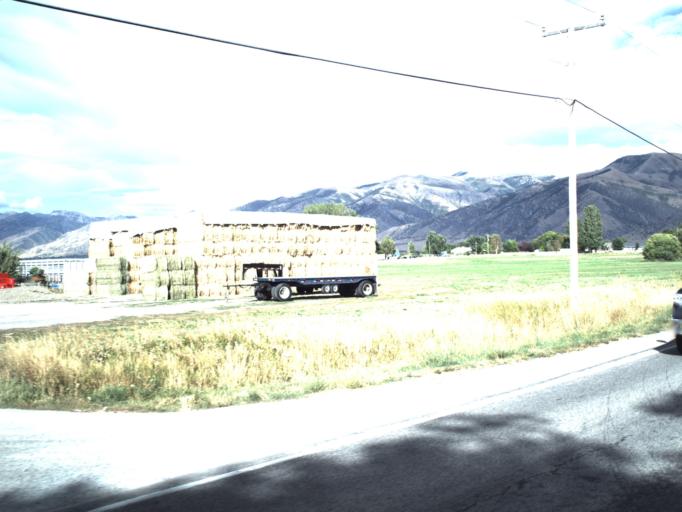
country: US
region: Utah
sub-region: Cache County
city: Hyrum
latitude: 41.6410
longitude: -111.8909
